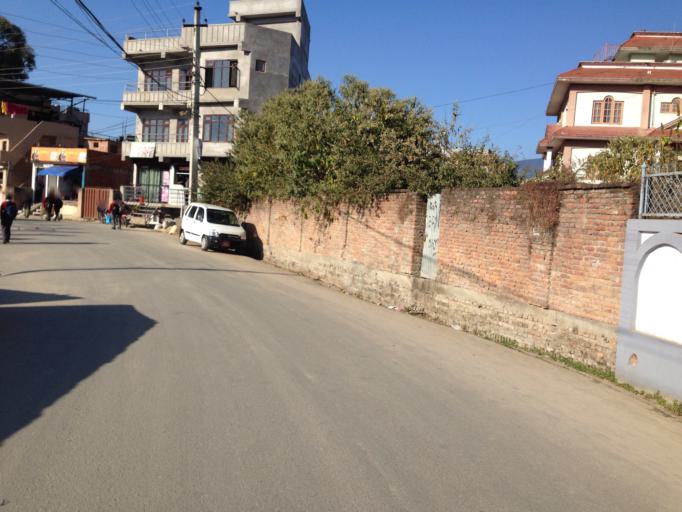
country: NP
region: Central Region
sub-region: Bagmati Zone
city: Kathmandu
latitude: 27.7262
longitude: 85.3358
